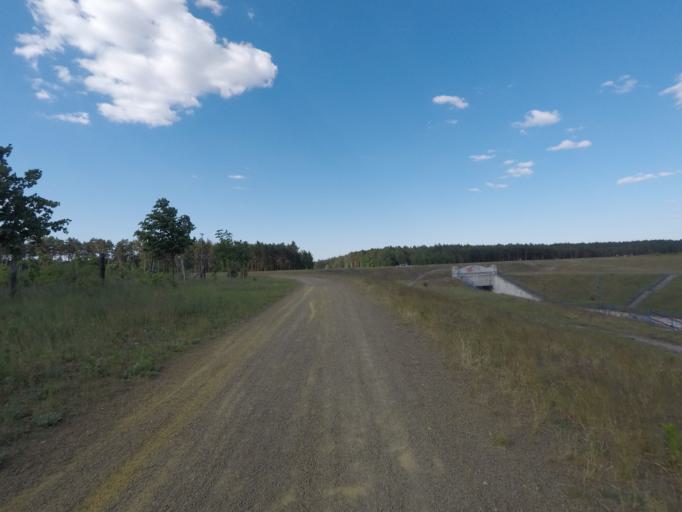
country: DE
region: Brandenburg
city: Eberswalde
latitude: 52.8535
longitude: 13.8039
